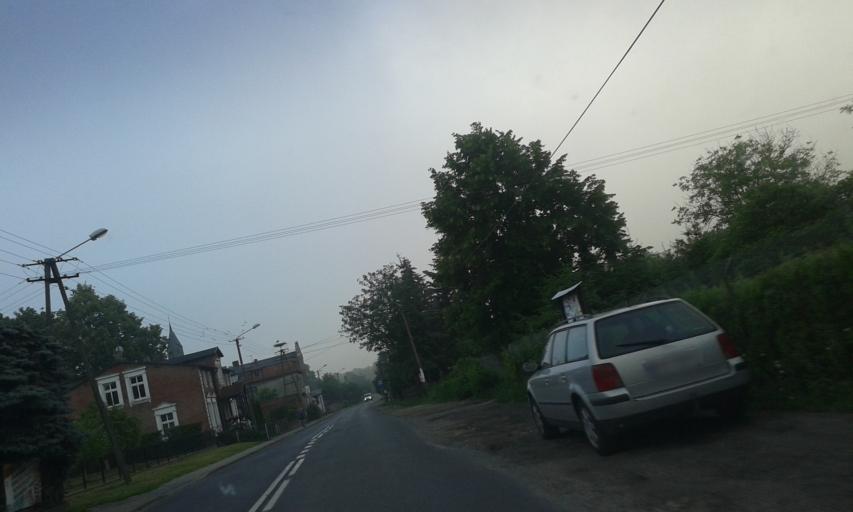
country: PL
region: Pomeranian Voivodeship
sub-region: Powiat czluchowski
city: Debrzno
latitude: 53.5282
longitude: 17.2313
